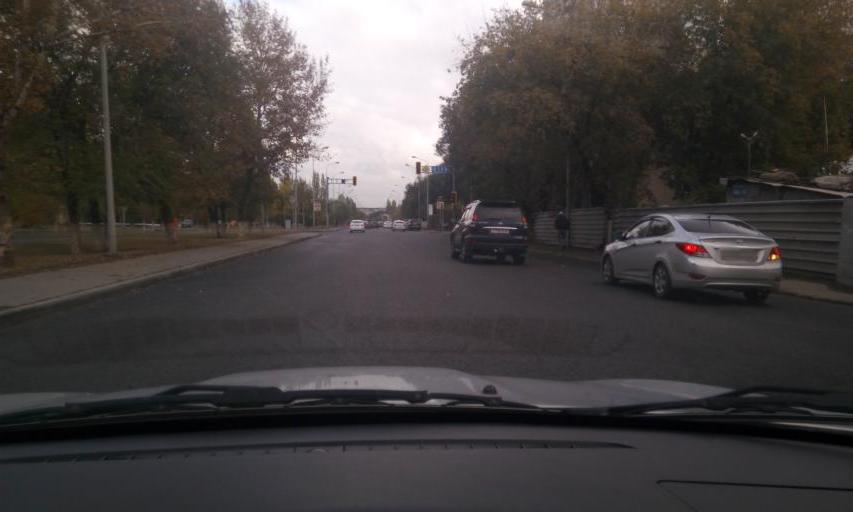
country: KZ
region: Astana Qalasy
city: Astana
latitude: 51.1655
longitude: 71.4652
